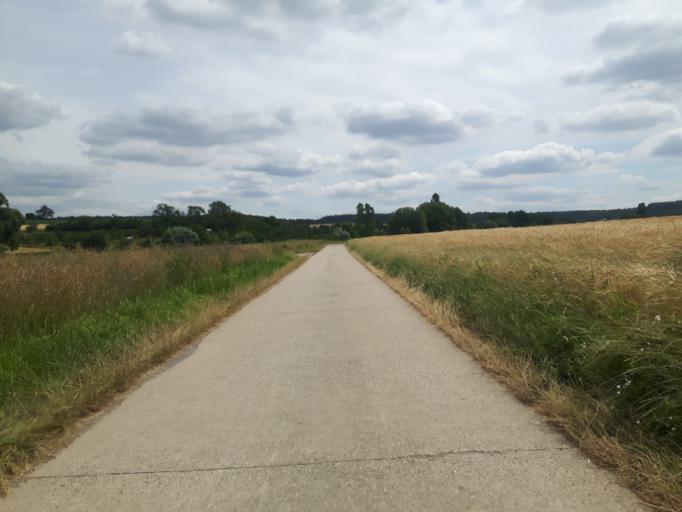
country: DE
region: Baden-Wuerttemberg
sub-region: Regierungsbezirk Stuttgart
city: Eppingen
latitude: 49.1109
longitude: 8.8930
